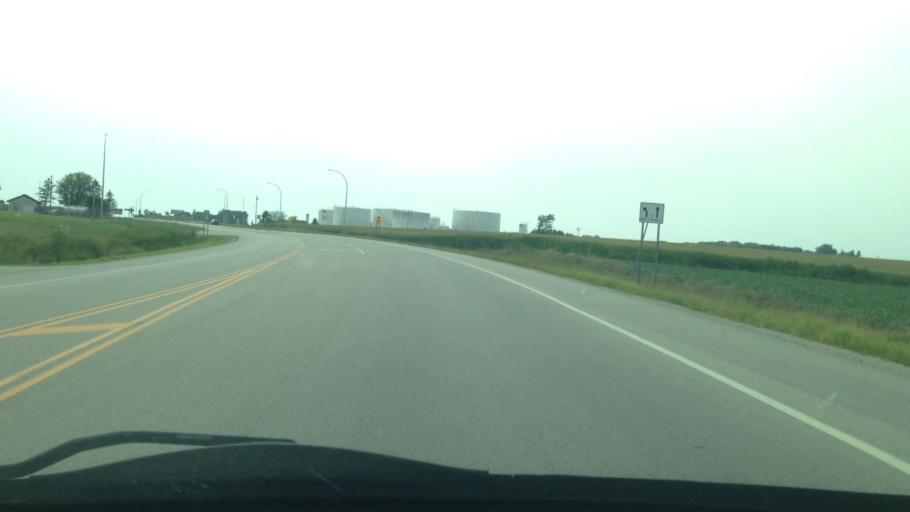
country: US
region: Minnesota
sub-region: Olmsted County
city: Eyota
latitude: 43.9989
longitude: -92.2443
